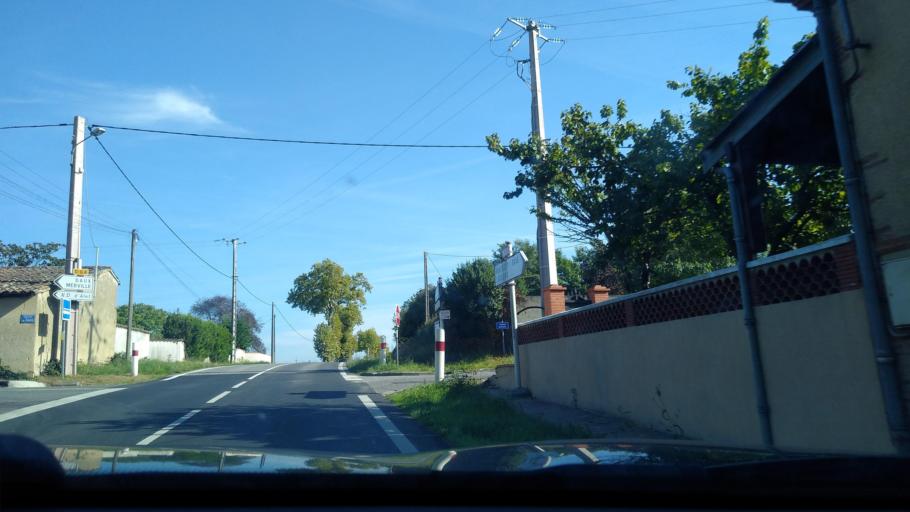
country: FR
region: Midi-Pyrenees
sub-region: Departement de la Haute-Garonne
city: Montaigut-sur-Save
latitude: 43.6875
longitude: 1.2413
